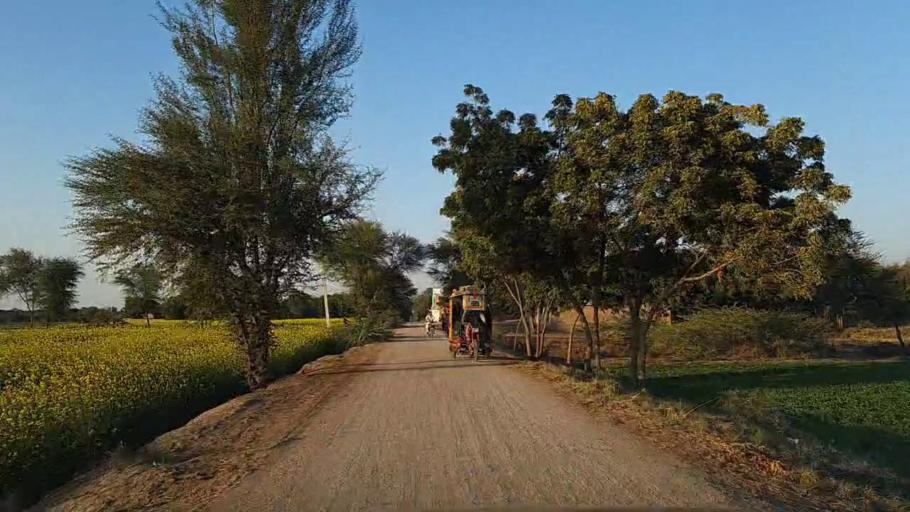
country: PK
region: Sindh
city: Nawabshah
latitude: 26.2384
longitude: 68.3382
